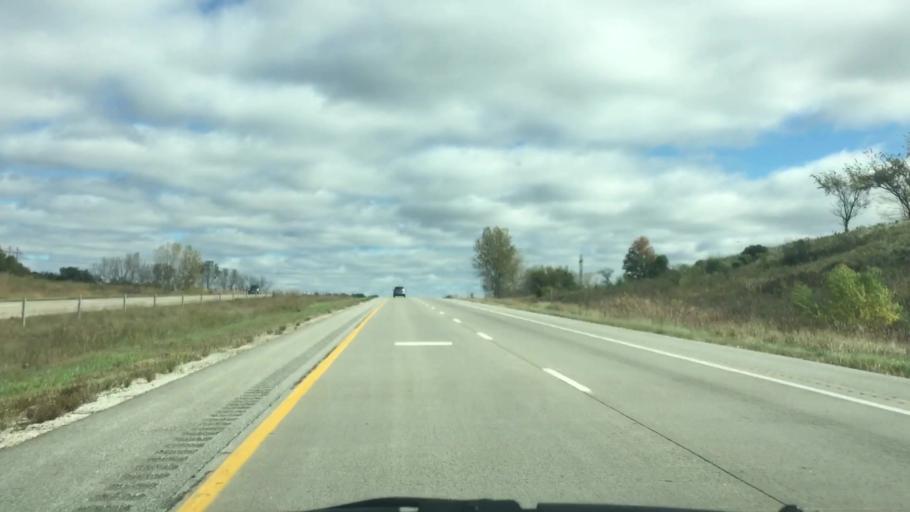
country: US
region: Iowa
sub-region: Jasper County
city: Newton
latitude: 41.6817
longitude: -93.0899
